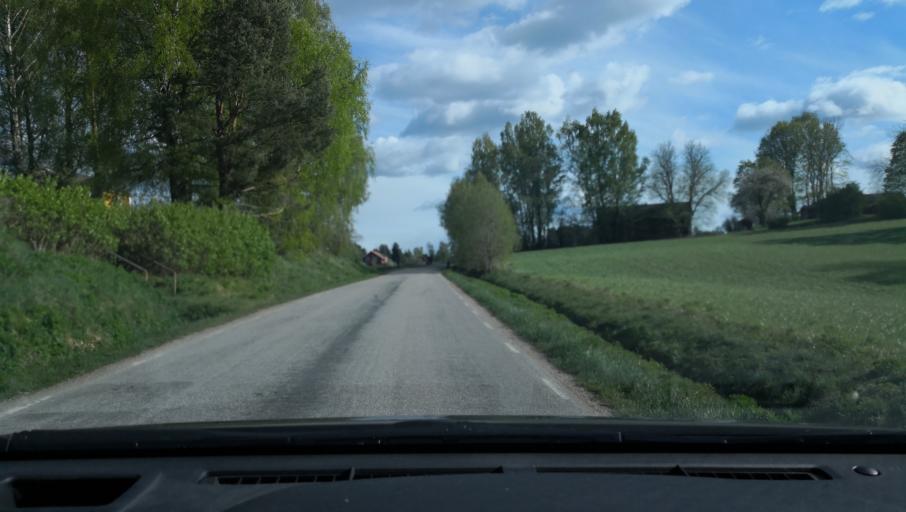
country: SE
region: OErebro
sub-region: Askersunds Kommun
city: Asbro
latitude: 58.9749
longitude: 15.0662
